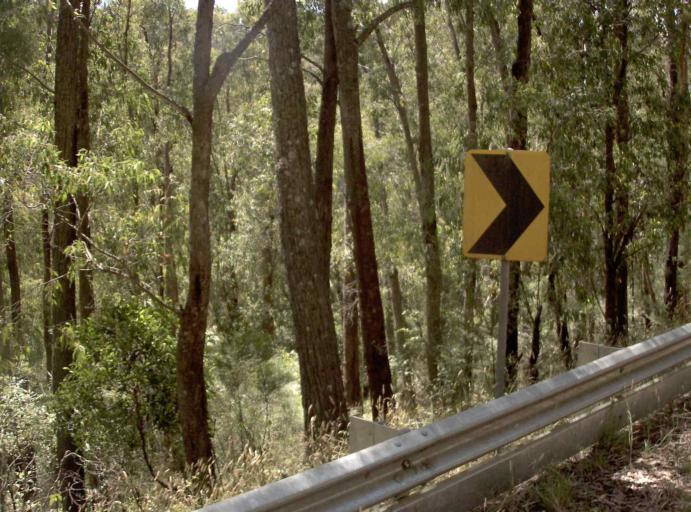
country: AU
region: Victoria
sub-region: Baw Baw
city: Warragul
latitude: -37.8929
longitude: 146.0279
